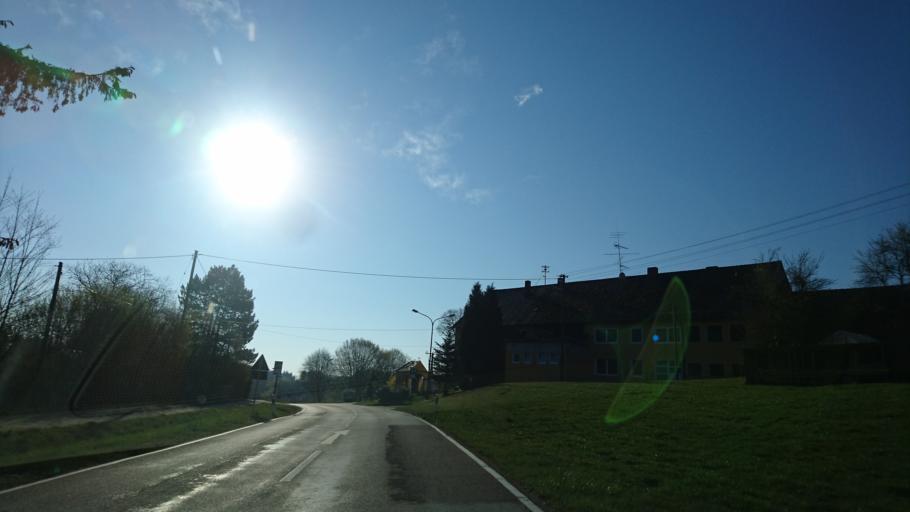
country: DE
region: Bavaria
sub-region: Swabia
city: Gablingen
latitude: 48.4435
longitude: 10.7792
